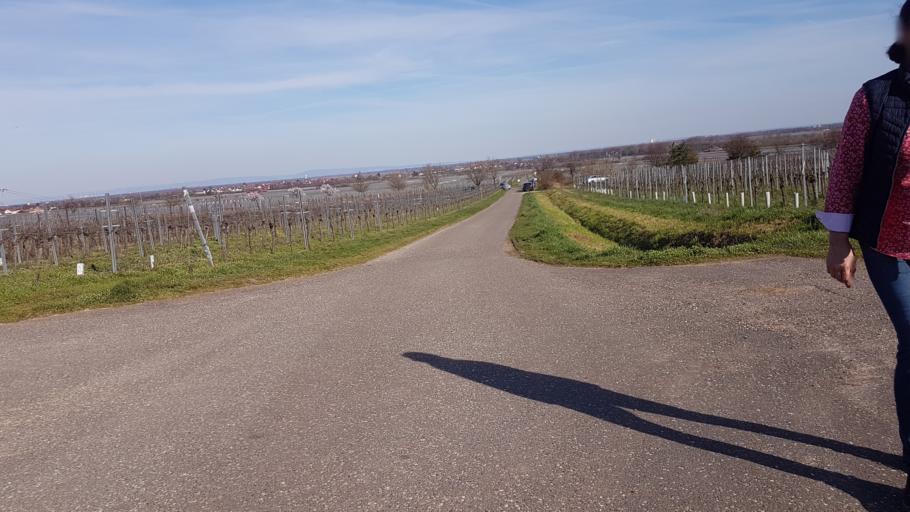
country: DE
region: Rheinland-Pfalz
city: Maikammer
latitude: 49.2961
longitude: 8.1293
